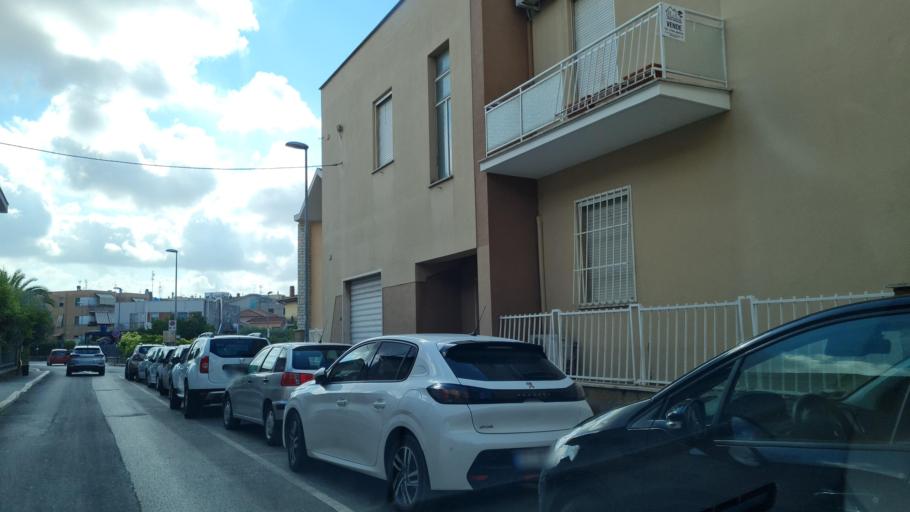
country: IT
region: Latium
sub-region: Provincia di Viterbo
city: Tarquinia
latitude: 42.2487
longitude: 11.7588
